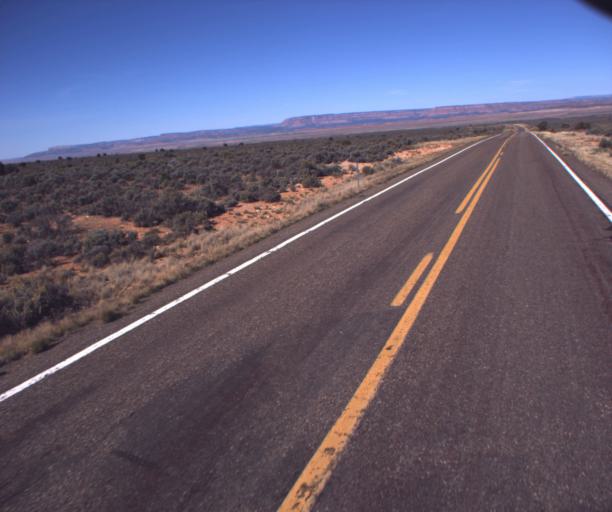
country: US
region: Arizona
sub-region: Coconino County
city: Fredonia
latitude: 36.8848
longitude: -112.3450
